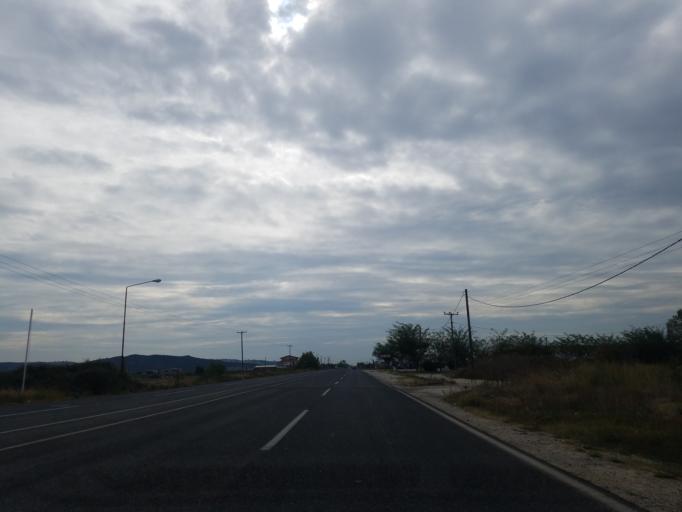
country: GR
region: Thessaly
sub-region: Trikala
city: Kalampaka
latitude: 39.6819
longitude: 21.6540
